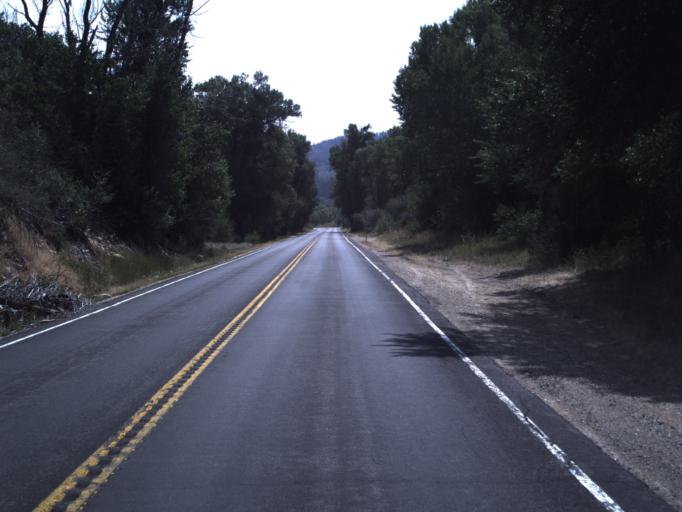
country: US
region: Utah
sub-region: Summit County
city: Francis
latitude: 40.5645
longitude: -111.1879
